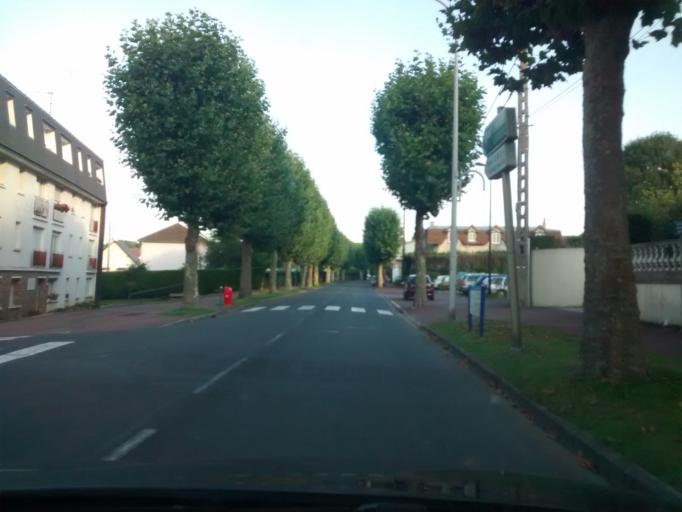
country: FR
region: Lower Normandy
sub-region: Departement du Calvados
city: Villers-sur-Mer
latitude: 49.3199
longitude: 0.0008
